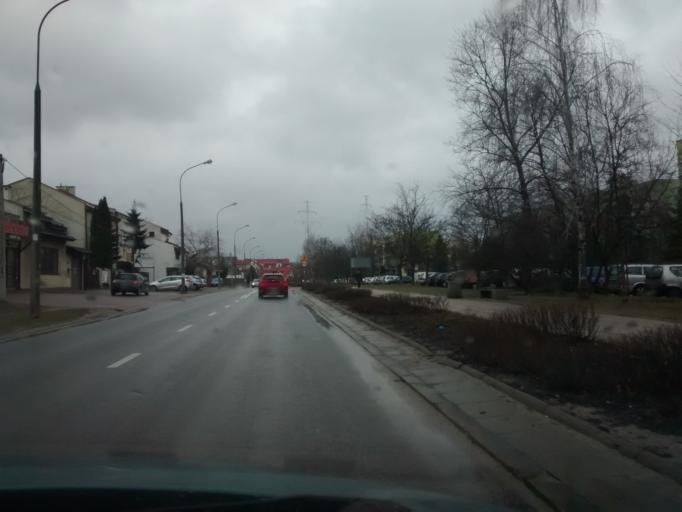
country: PL
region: Masovian Voivodeship
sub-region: Warszawa
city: Bialoleka
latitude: 52.3193
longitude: 20.9448
